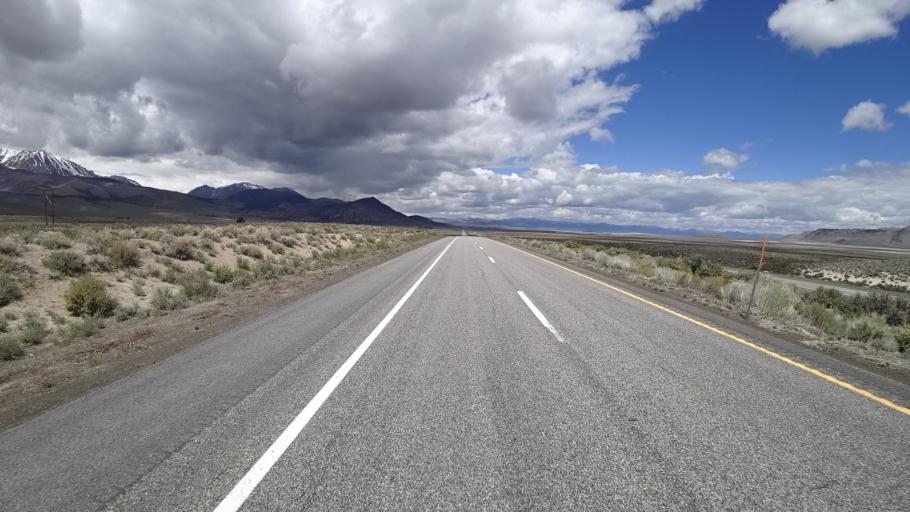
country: US
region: California
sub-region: Mono County
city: Mammoth Lakes
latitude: 37.8674
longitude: -119.0876
